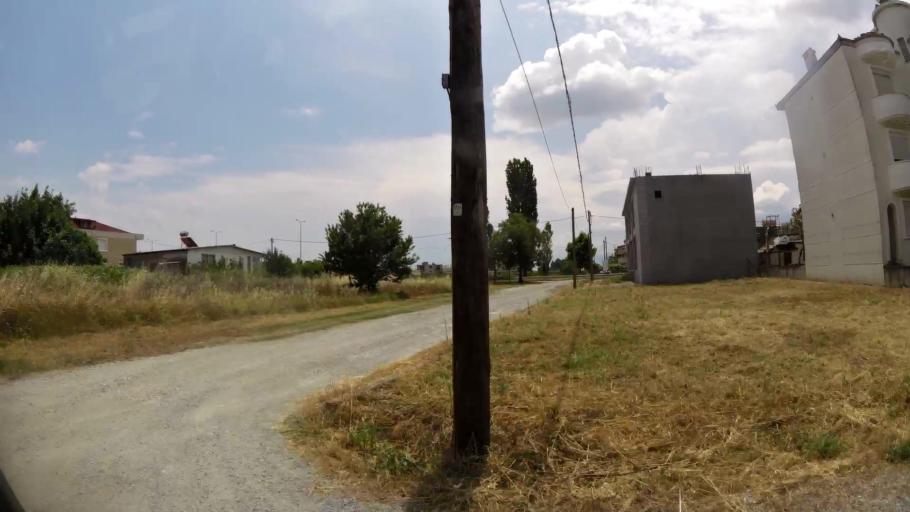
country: GR
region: Central Macedonia
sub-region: Nomos Pierias
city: Peristasi
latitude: 40.2743
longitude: 22.5467
